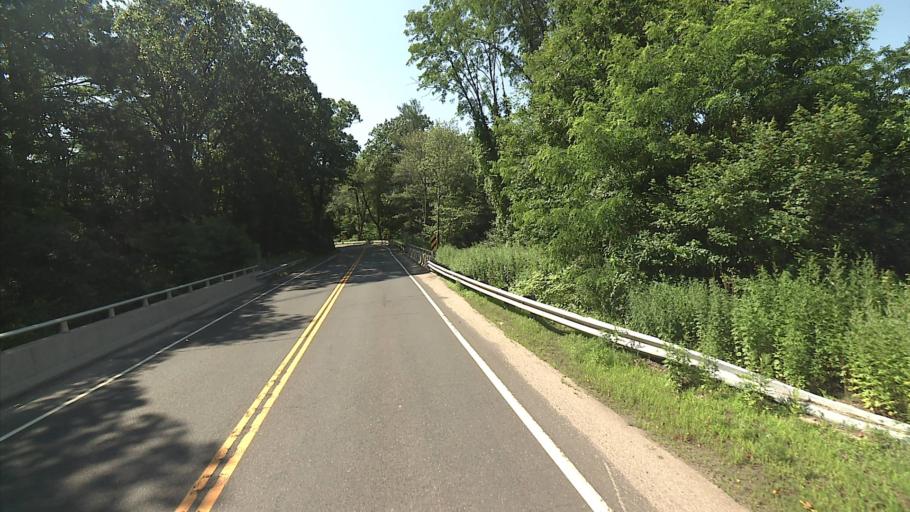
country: US
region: Connecticut
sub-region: Litchfield County
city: Terryville
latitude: 41.6915
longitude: -73.0047
